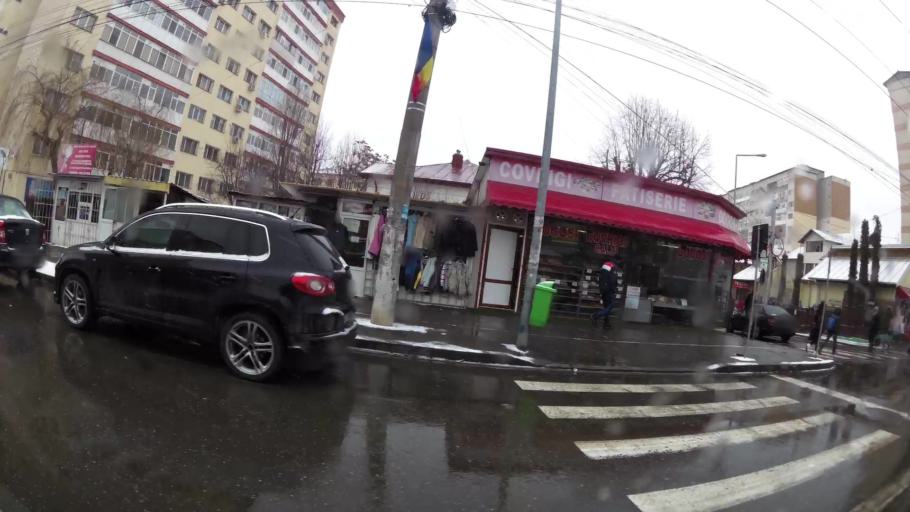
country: RO
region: Dambovita
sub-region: Municipiul Targoviste
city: Targoviste
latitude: 44.9204
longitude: 25.4502
